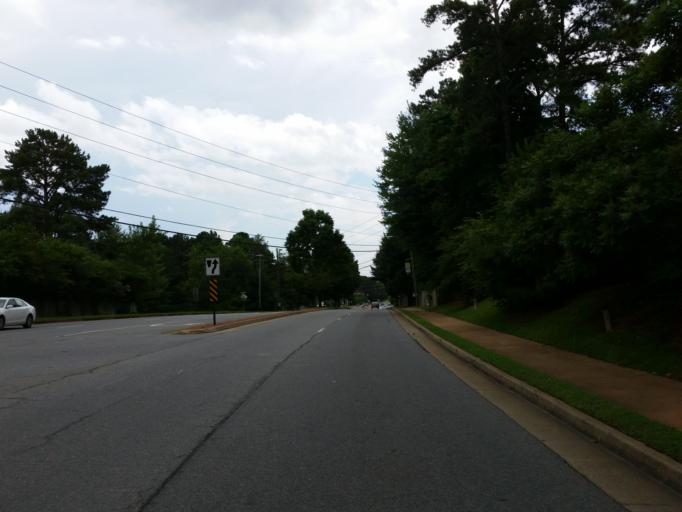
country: US
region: Georgia
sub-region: Cobb County
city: Kennesaw
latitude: 34.0693
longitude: -84.5874
